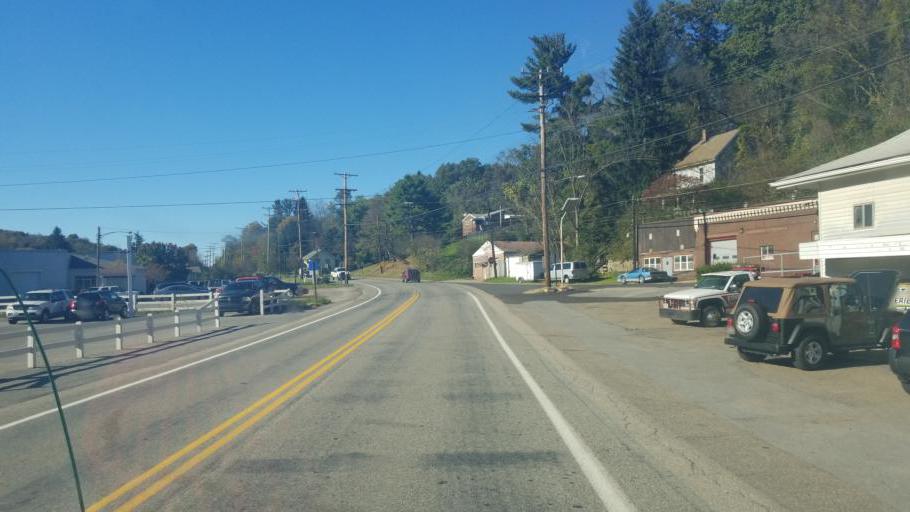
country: US
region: Pennsylvania
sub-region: Allegheny County
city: Imperial
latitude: 40.4516
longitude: -80.2515
